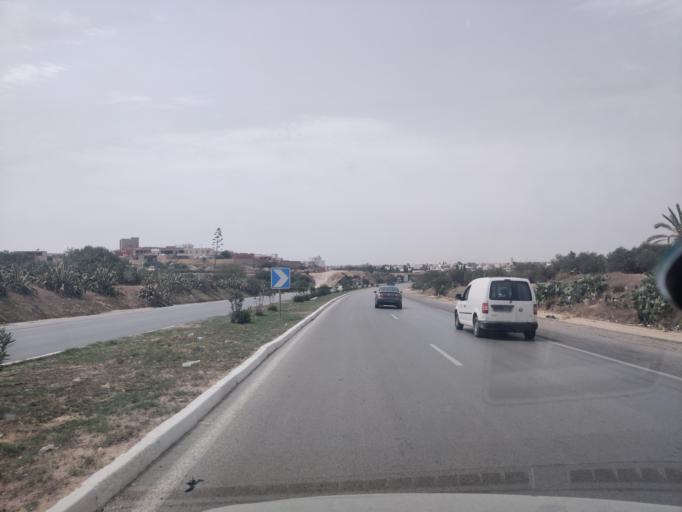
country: TN
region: Susah
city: Akouda
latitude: 35.8342
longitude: 10.5721
